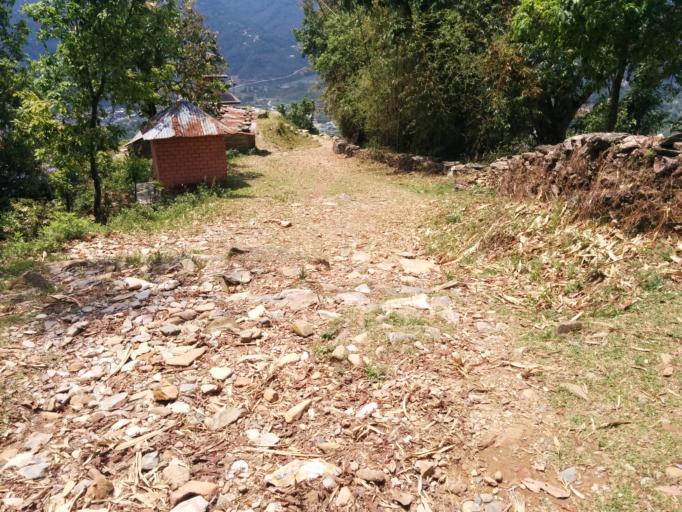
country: NP
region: Western Region
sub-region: Gandaki Zone
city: Pokhara
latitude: 28.1973
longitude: 83.9510
